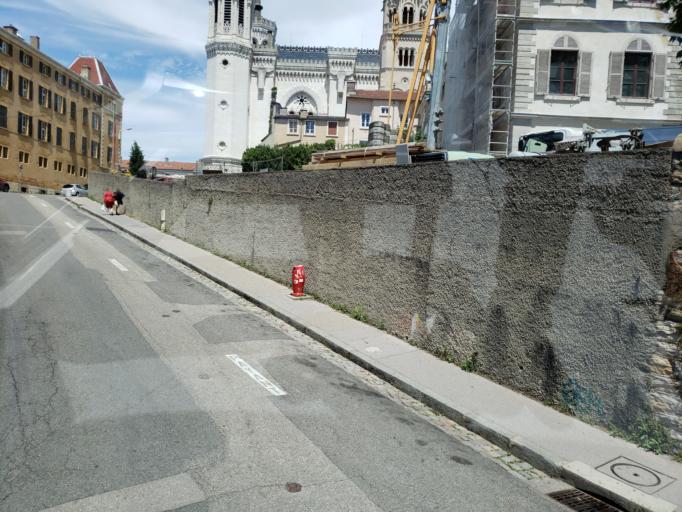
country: FR
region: Rhone-Alpes
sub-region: Departement du Rhone
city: Lyon
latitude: 45.7613
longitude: 4.8221
